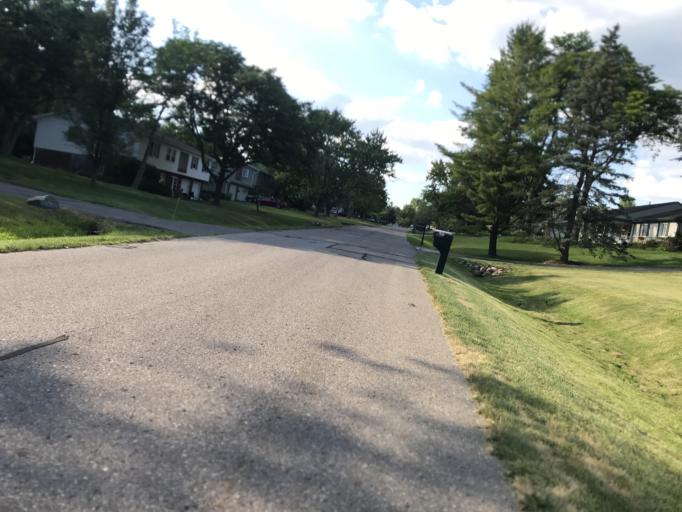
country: US
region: Michigan
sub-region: Oakland County
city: Farmington
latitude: 42.4665
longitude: -83.3234
